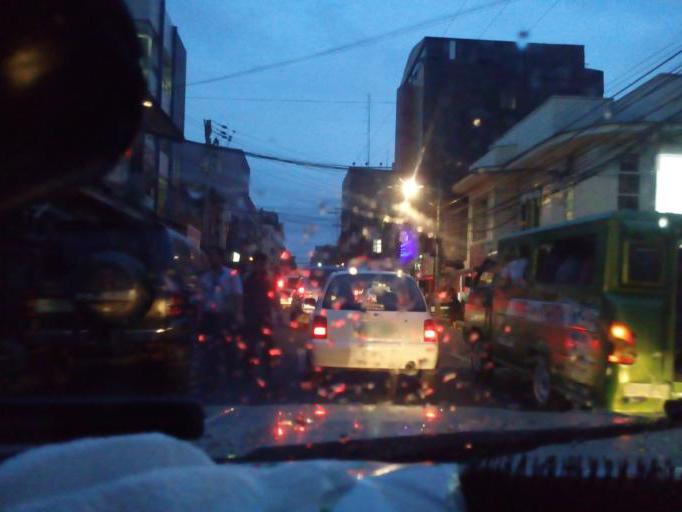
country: PH
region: Central Visayas
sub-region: Cebu City
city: Calero
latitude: 10.3016
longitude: 123.8984
